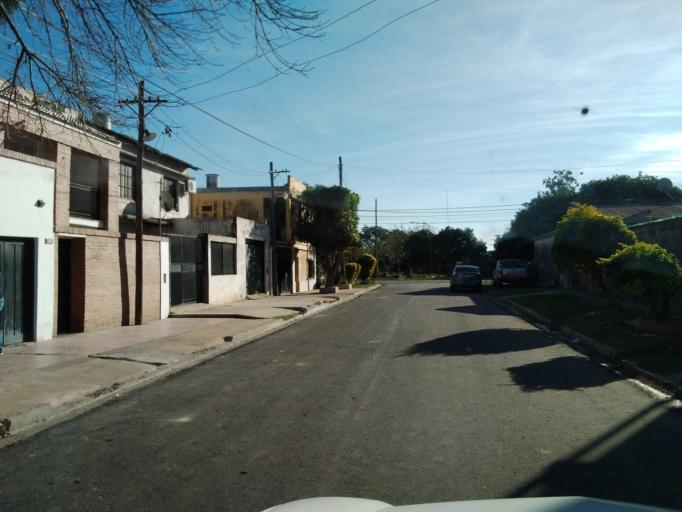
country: AR
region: Corrientes
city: Corrientes
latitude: -27.4937
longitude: -58.8392
